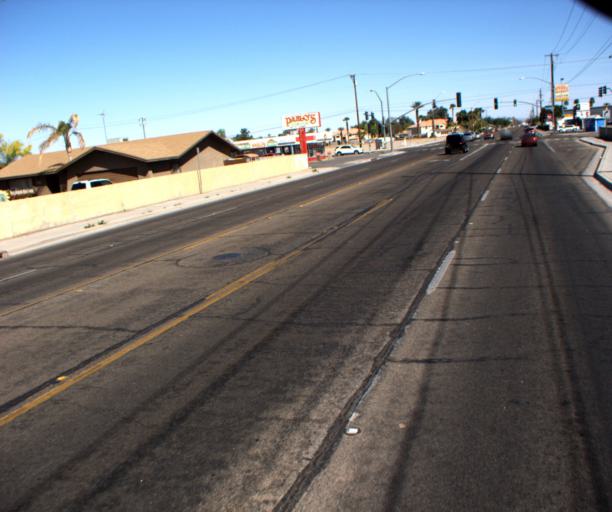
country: US
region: Arizona
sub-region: Yuma County
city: Yuma
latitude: 32.6903
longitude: -114.6504
